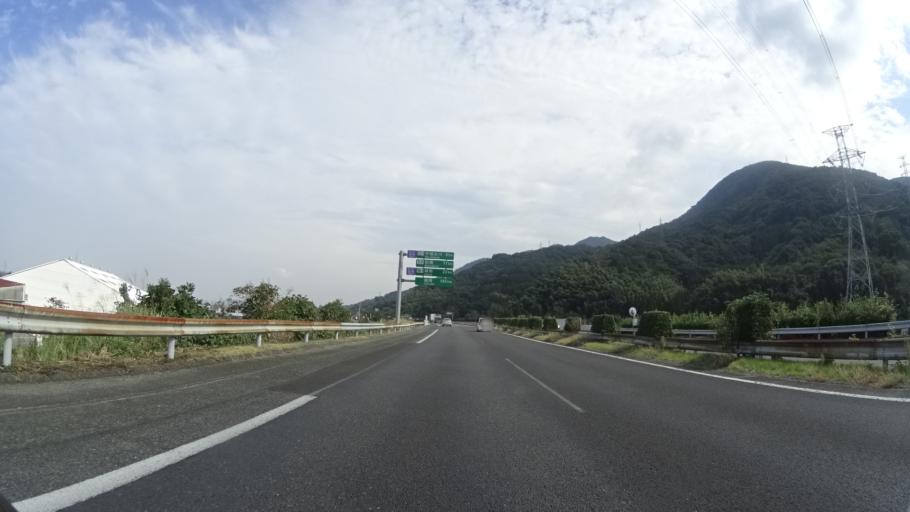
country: JP
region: Kumamoto
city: Yatsushiro
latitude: 32.5215
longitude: 130.6567
